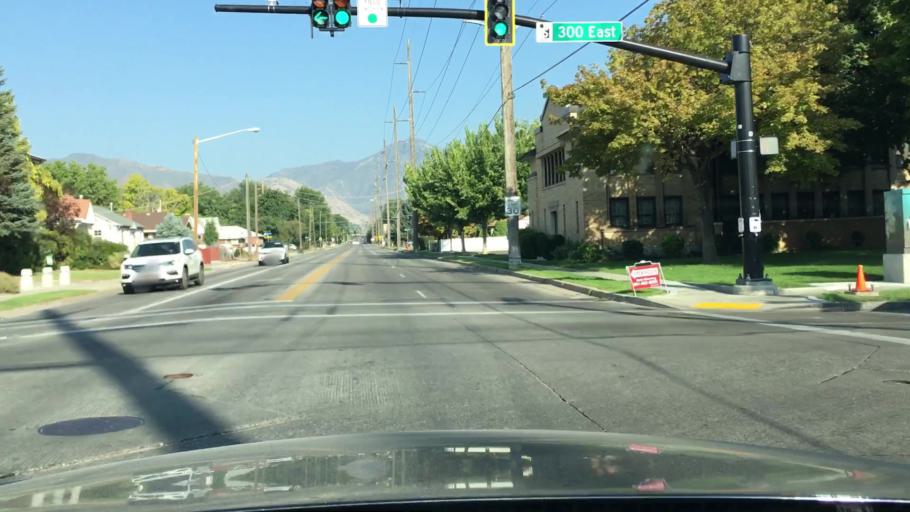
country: US
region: Utah
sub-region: Salt Lake County
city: South Salt Lake
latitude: 40.7126
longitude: -111.8827
